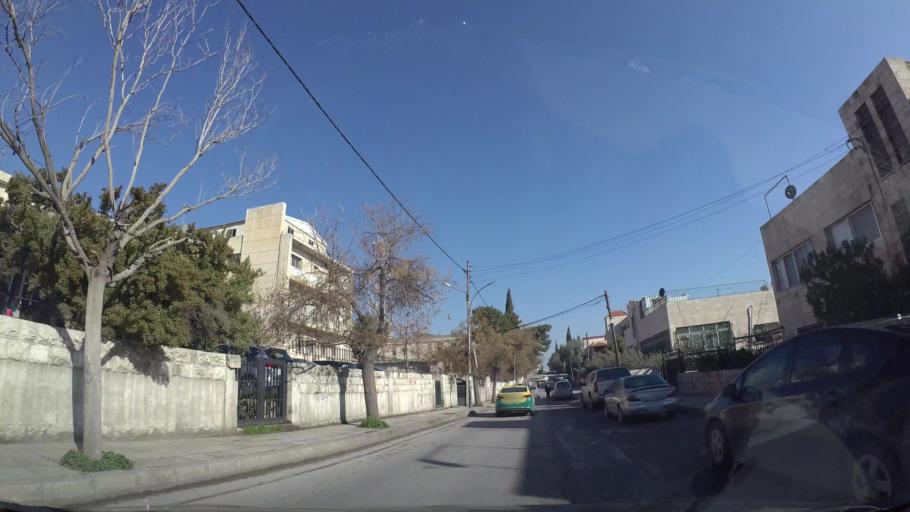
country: JO
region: Amman
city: Amman
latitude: 31.9831
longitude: 35.9893
